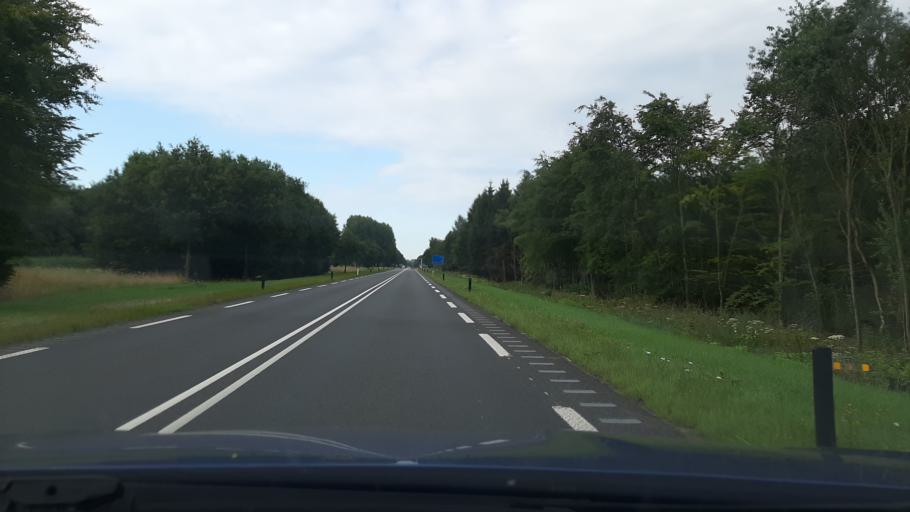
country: NL
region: Flevoland
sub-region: Gemeente Zeewolde
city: Zeewolde
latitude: 52.3132
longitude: 5.5193
